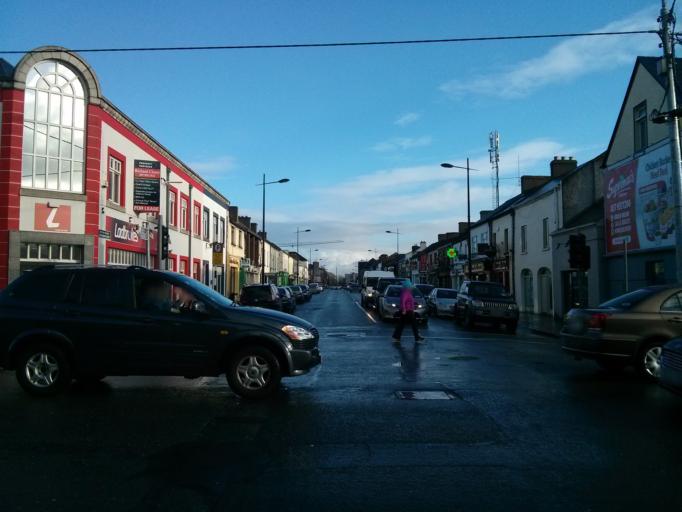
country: IE
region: Leinster
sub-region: Uibh Fhaili
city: Tullamore
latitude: 53.2764
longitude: -7.4920
